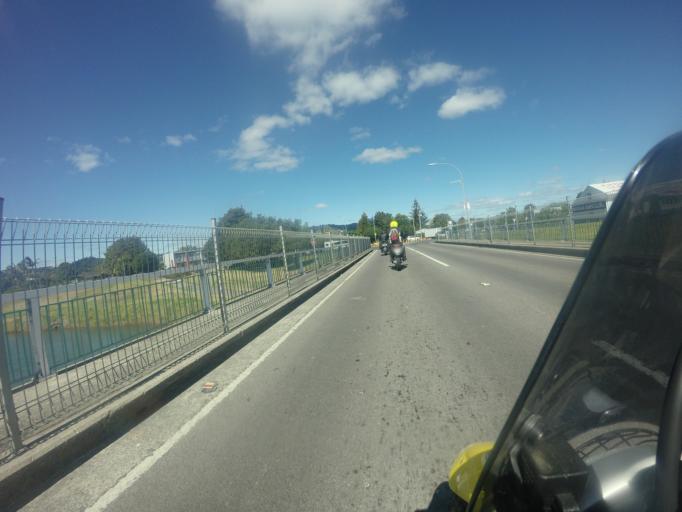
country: NZ
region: Bay of Plenty
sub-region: Whakatane District
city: Whakatane
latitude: -37.9577
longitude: 176.9734
